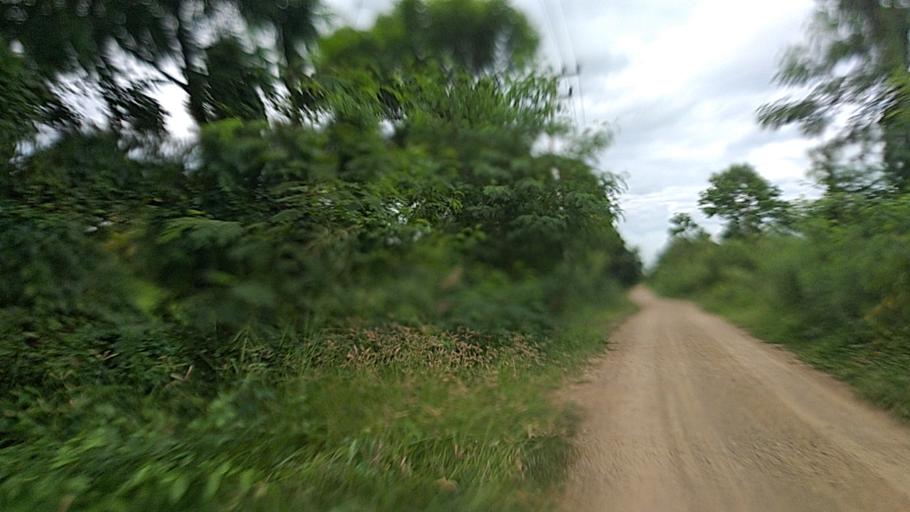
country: TH
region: Pathum Thani
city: Nong Suea
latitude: 14.0762
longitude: 100.8363
